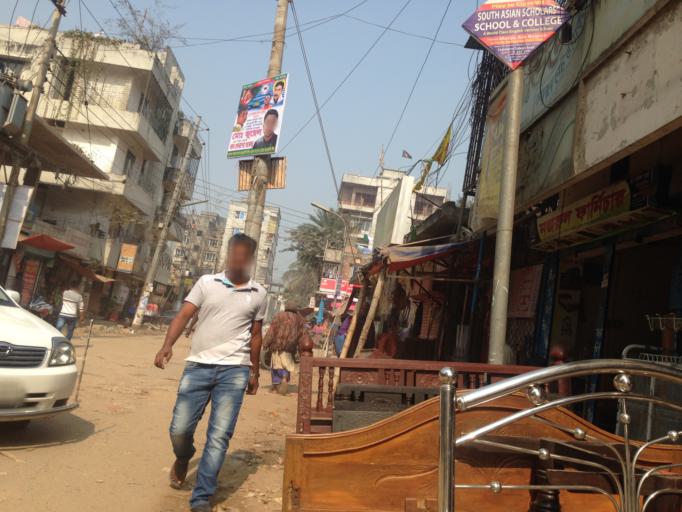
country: BD
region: Dhaka
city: Azimpur
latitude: 23.8045
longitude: 90.3477
